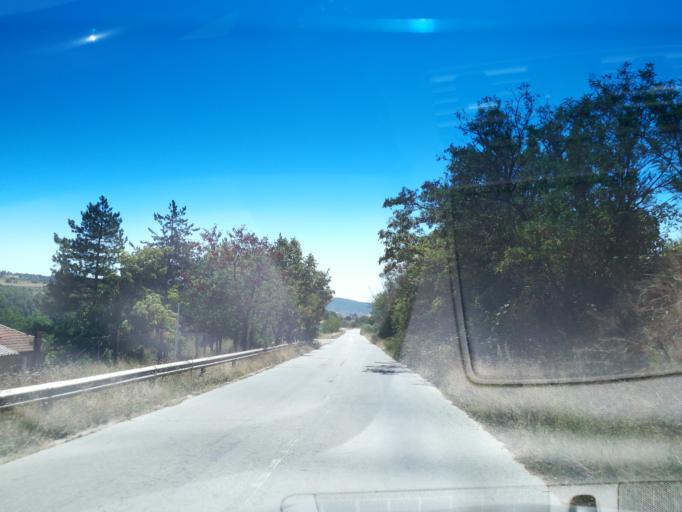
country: BG
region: Pazardzhik
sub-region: Obshtina Strelcha
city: Strelcha
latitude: 42.5206
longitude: 24.3216
